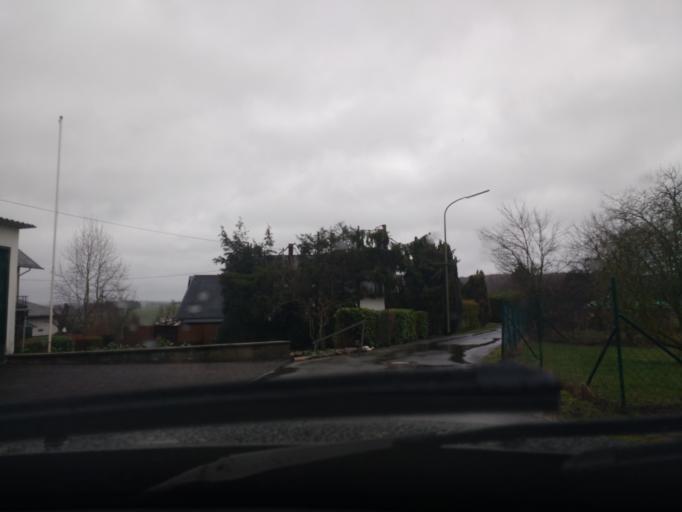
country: DE
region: Rheinland-Pfalz
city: Lotzbeuren
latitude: 49.9349
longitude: 7.2242
